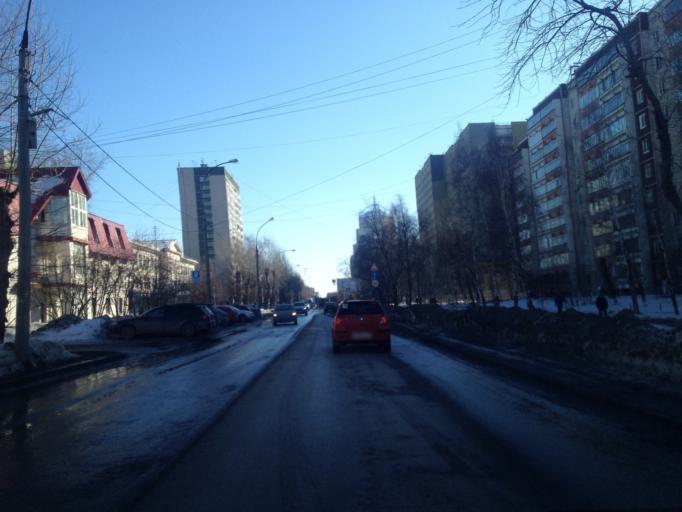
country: RU
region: Sverdlovsk
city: Yekaterinburg
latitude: 56.8398
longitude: 60.6601
